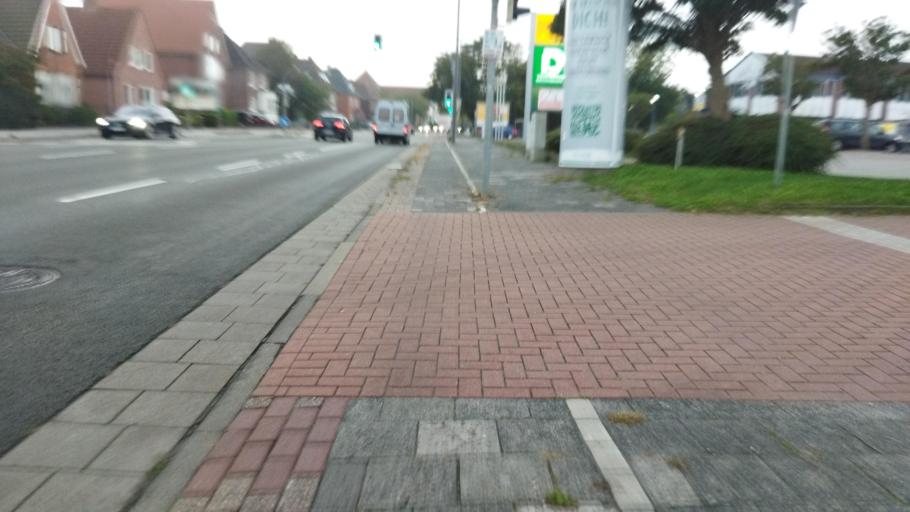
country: DE
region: Lower Saxony
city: Emden
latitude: 53.3856
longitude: 7.2076
